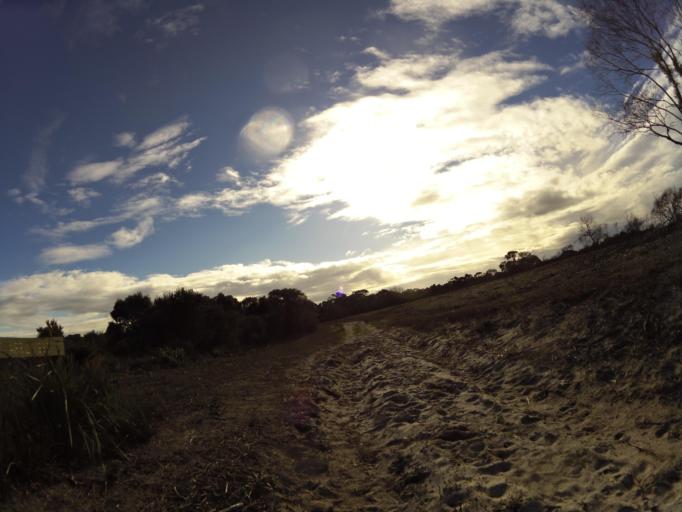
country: AU
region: Victoria
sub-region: Bass Coast
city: North Wonthaggi
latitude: -38.6353
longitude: 145.5676
